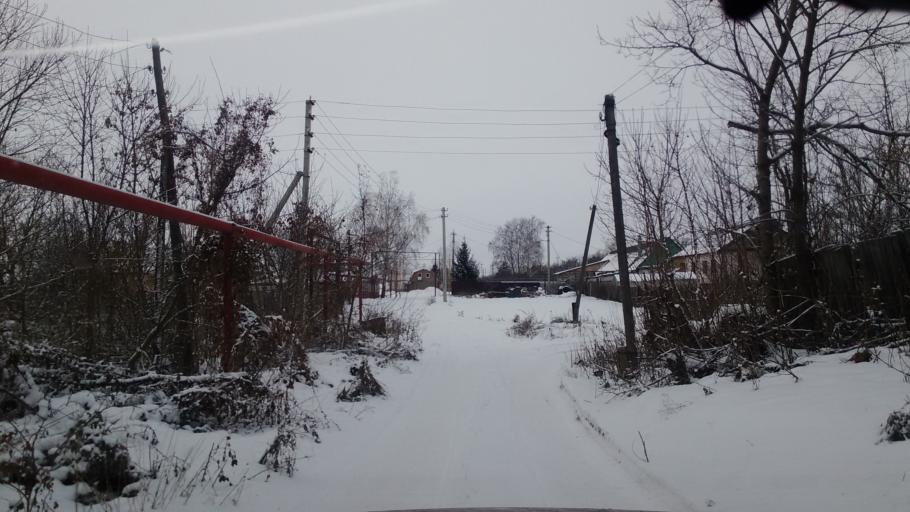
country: RU
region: Tula
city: Bogoroditsk
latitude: 53.7574
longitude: 38.1175
